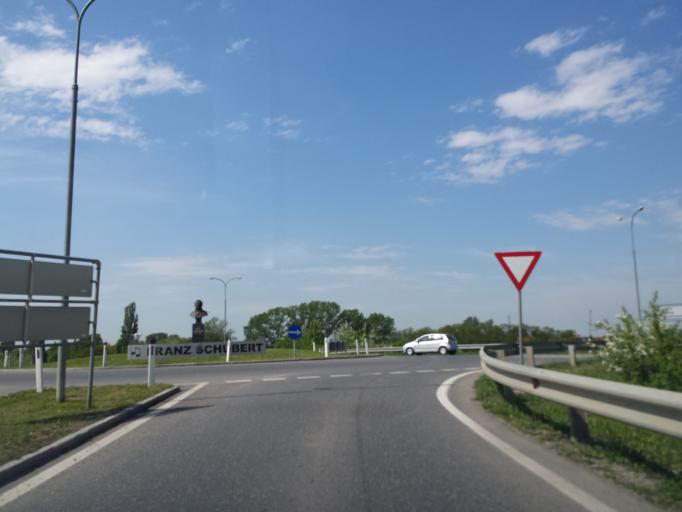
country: AT
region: Lower Austria
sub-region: Politischer Bezirk Tulln
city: Atzenbrugg
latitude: 48.2881
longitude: 15.9124
